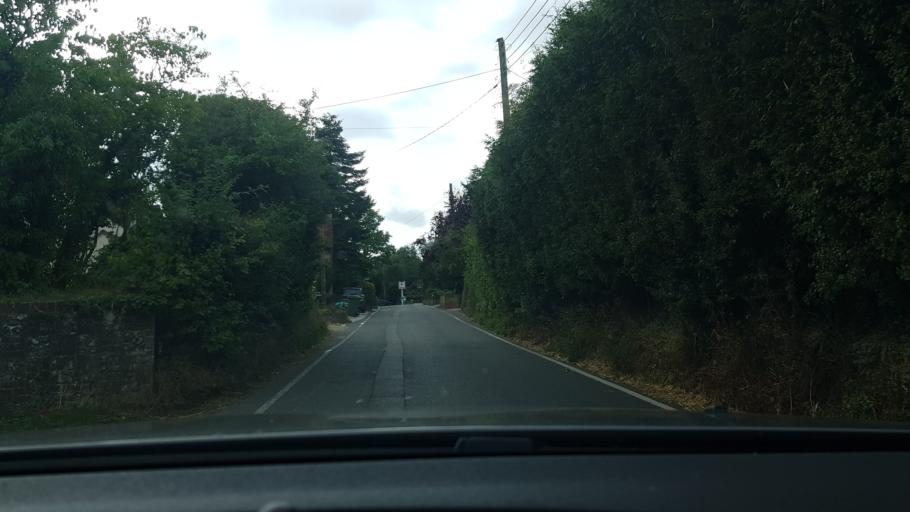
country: GB
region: England
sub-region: West Berkshire
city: Winterbourne
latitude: 51.4609
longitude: -1.3132
